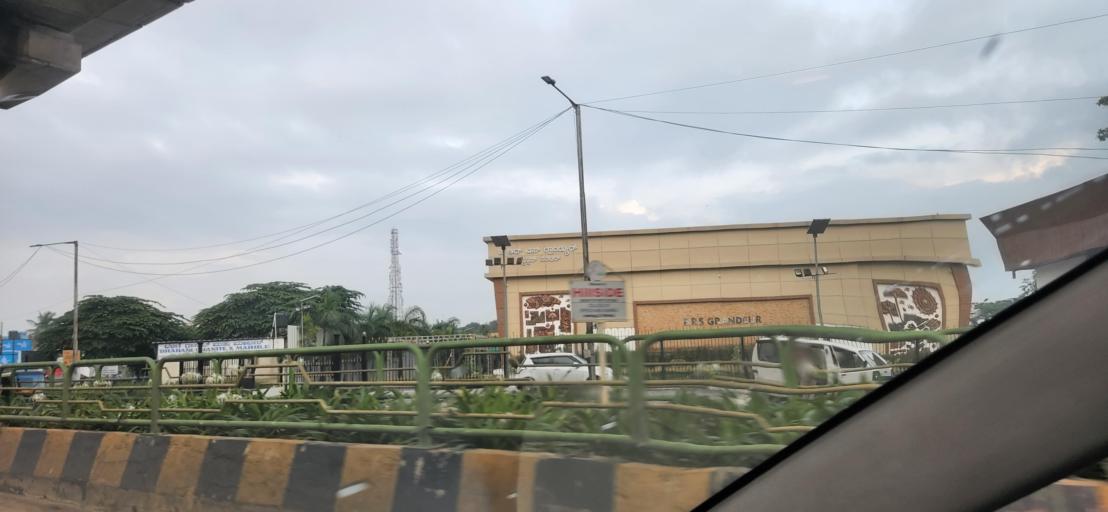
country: IN
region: Karnataka
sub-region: Bangalore Urban
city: Bangalore
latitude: 12.8725
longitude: 77.5392
